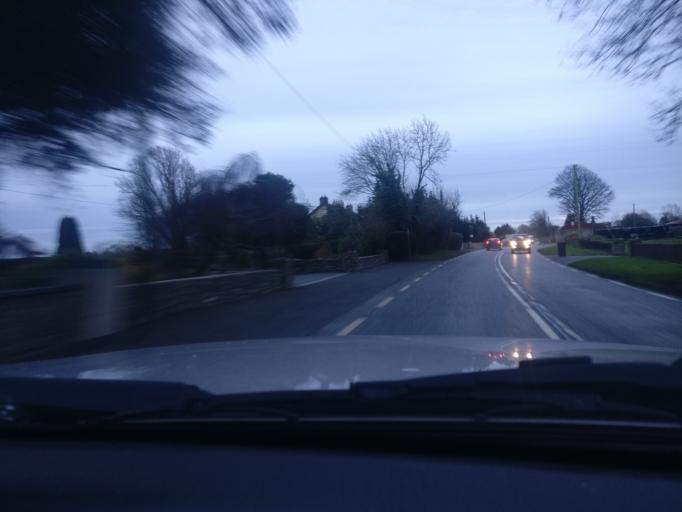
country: IE
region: Leinster
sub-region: An Mhi
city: Kells
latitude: 53.7170
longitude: -6.8329
